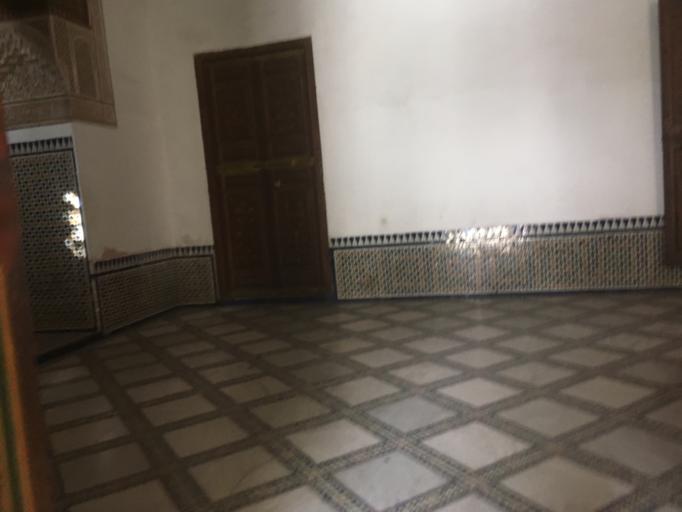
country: MA
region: Marrakech-Tensift-Al Haouz
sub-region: Marrakech
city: Marrakesh
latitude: 31.6214
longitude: -7.9821
